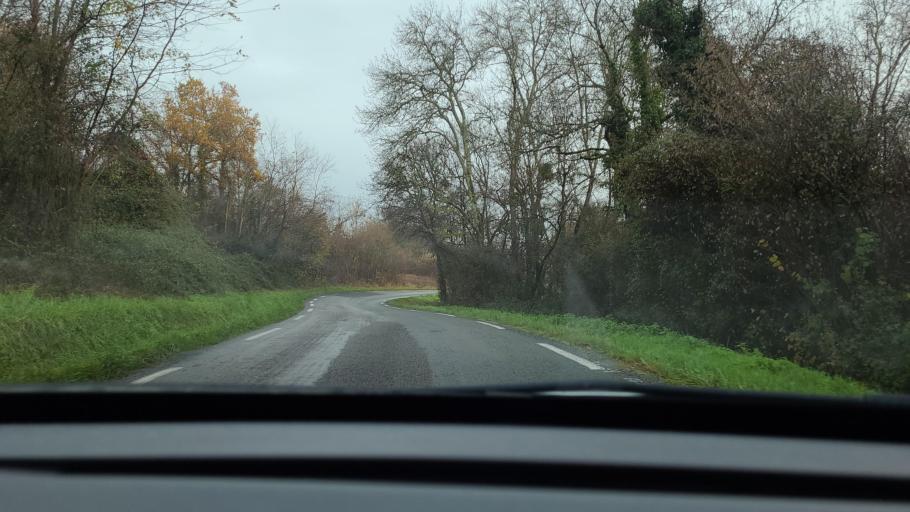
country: FR
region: Aquitaine
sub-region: Departement de la Gironde
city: Tauriac
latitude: 45.0433
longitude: -0.5066
